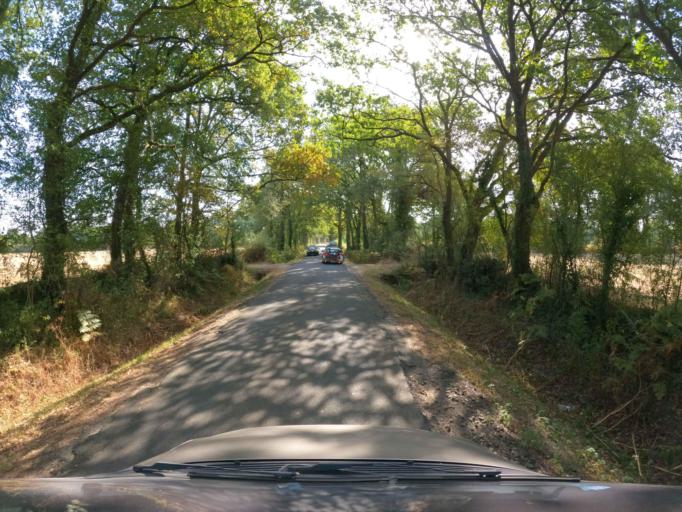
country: FR
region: Pays de la Loire
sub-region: Departement de la Vendee
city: Challans
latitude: 46.8077
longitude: -1.8608
